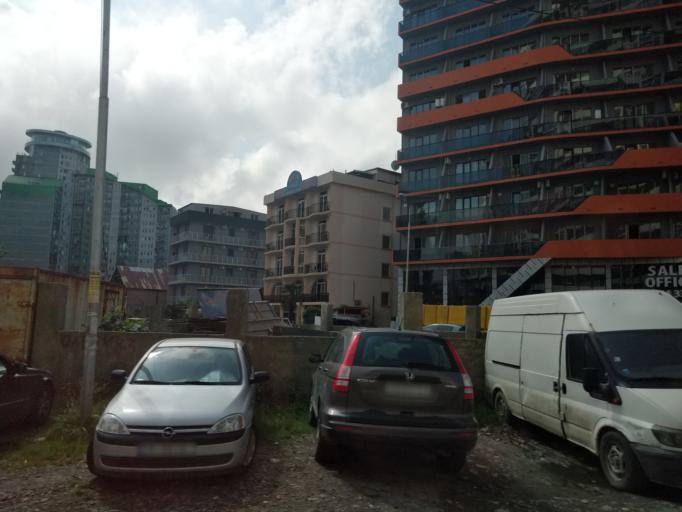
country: GE
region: Ajaria
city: Batumi
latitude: 41.6336
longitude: 41.6088
